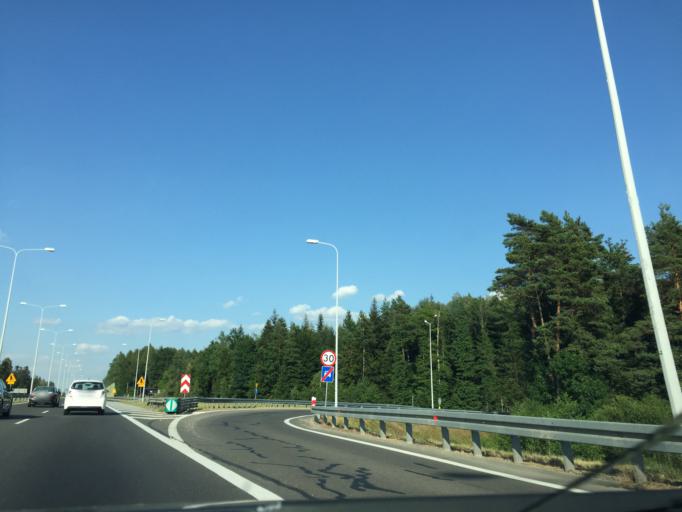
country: PL
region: Swietokrzyskie
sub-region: Powiat kielecki
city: Zagnansk
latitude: 50.9580
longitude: 20.7136
